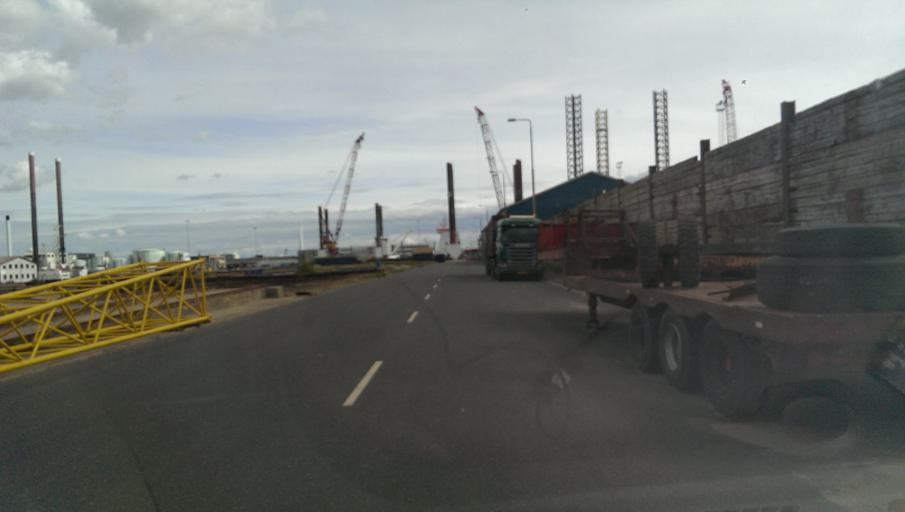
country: DK
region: South Denmark
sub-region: Fano Kommune
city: Nordby
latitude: 55.4796
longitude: 8.4145
